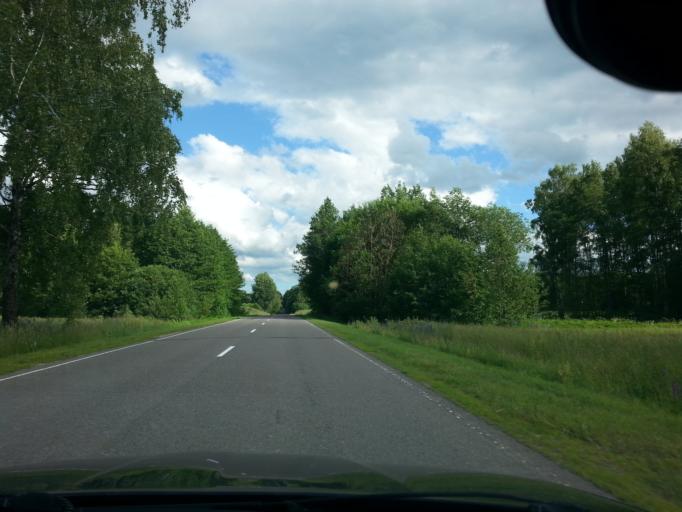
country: BY
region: Minsk
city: Svir
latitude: 54.9318
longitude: 26.3835
